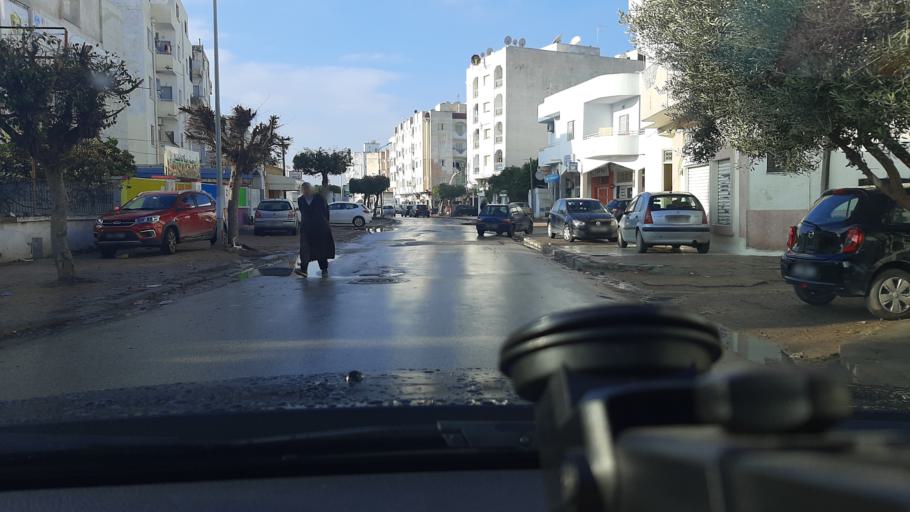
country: TN
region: Safaqis
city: Sfax
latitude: 34.7432
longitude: 10.7503
